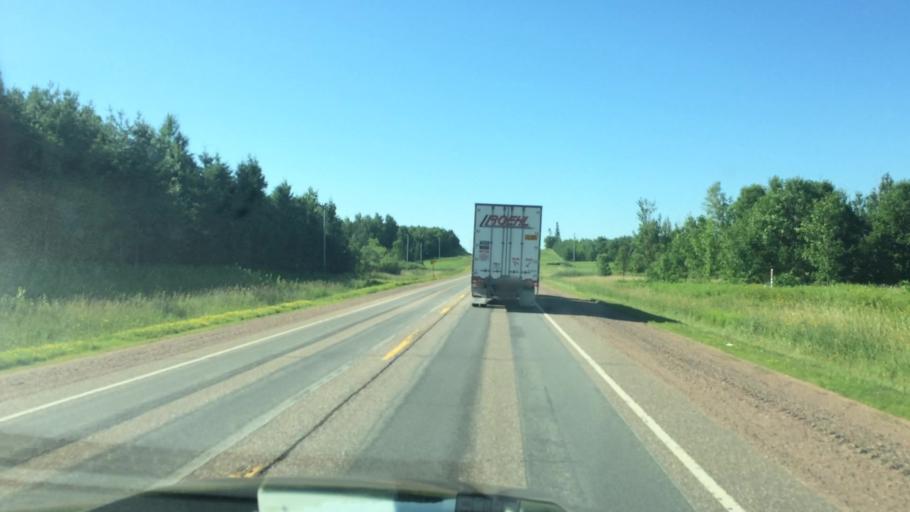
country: US
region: Wisconsin
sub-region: Marathon County
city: Athens
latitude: 44.9295
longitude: -90.0789
